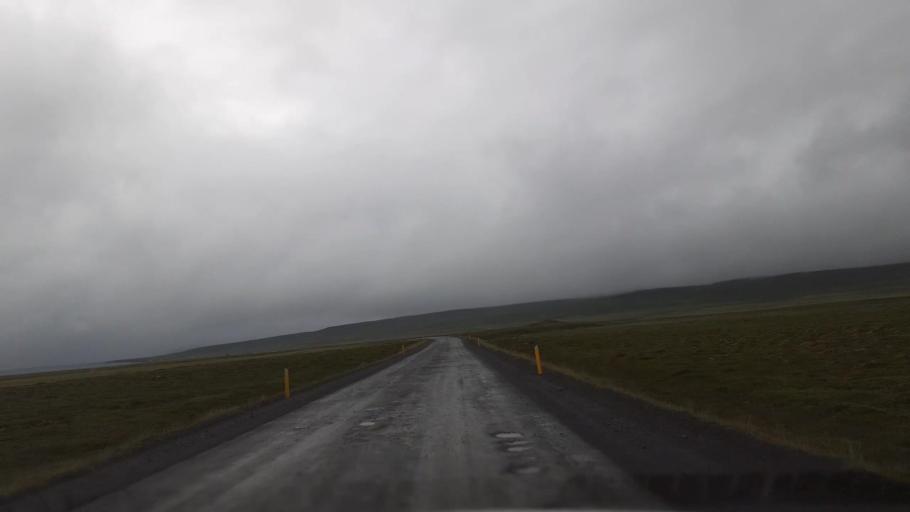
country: IS
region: East
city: Egilsstadir
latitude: 66.0342
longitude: -15.0600
